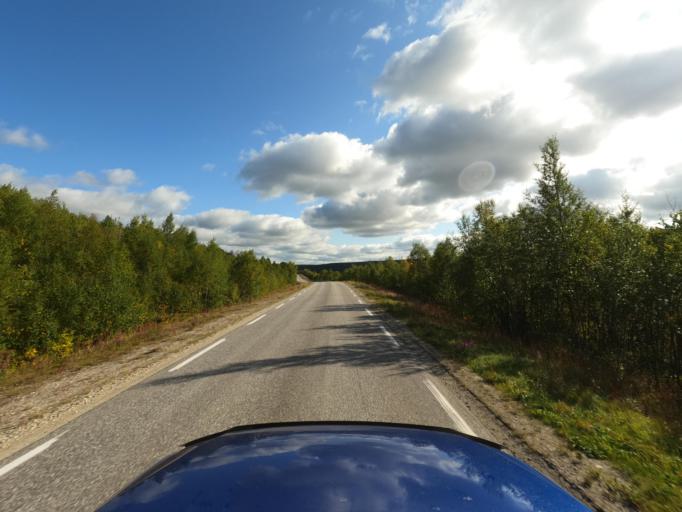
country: NO
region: Finnmark Fylke
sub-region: Porsanger
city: Lakselv
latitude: 69.4218
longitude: 24.8002
